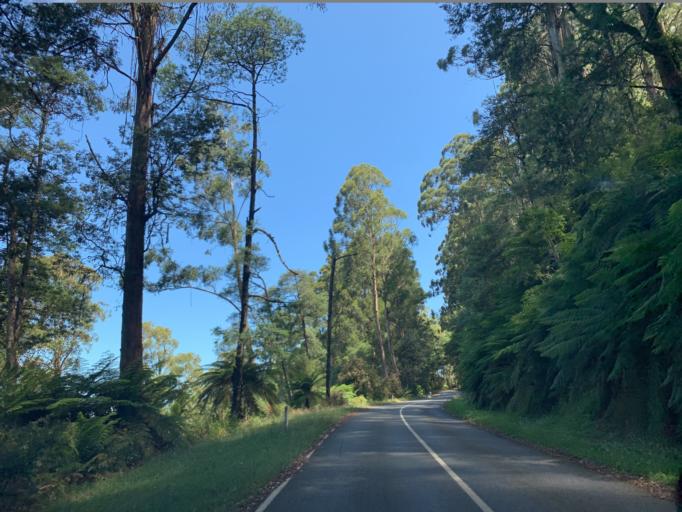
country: AU
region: Victoria
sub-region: Yarra Ranges
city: Millgrove
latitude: -37.7275
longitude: 145.7142
